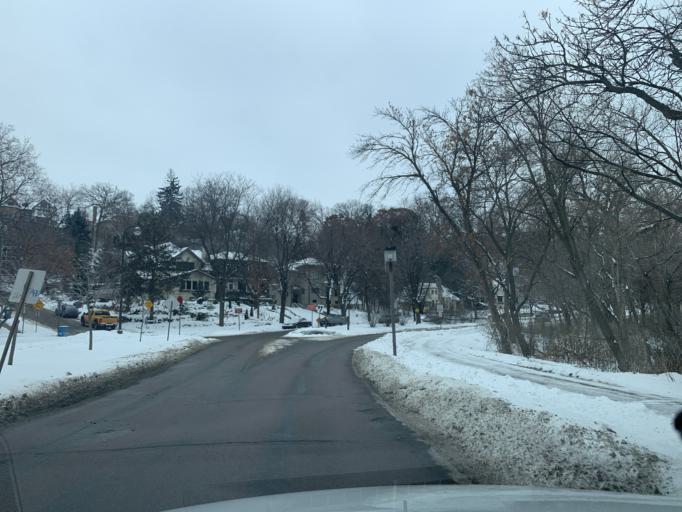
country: US
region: Minnesota
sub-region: Hennepin County
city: Minneapolis
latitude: 44.9695
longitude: -93.2961
